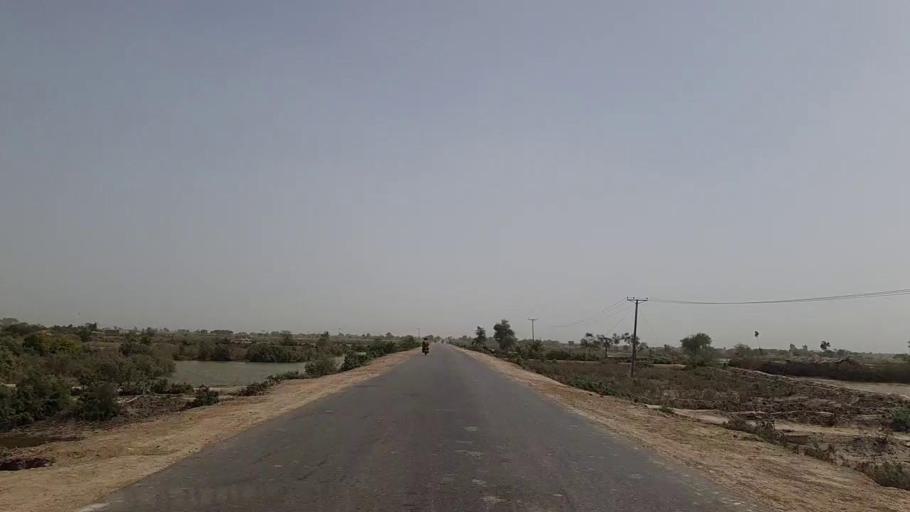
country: PK
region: Sindh
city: Talhar
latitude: 24.8670
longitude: 68.8442
